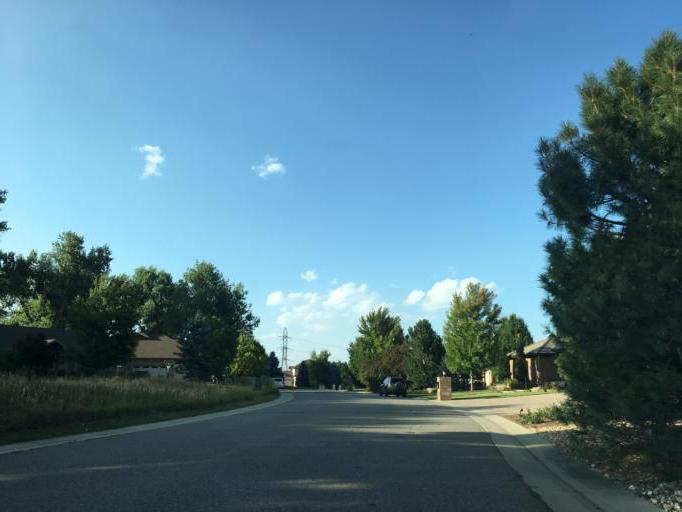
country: US
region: Colorado
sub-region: Jefferson County
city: Applewood
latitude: 39.7951
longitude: -105.1694
